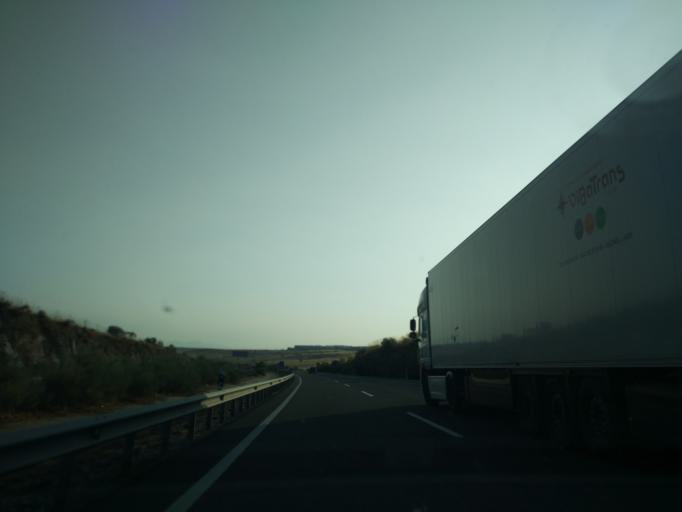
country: ES
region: Castille and Leon
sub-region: Provincia de Avila
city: Berrocalejo de Aragona
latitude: 40.6870
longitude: -4.5948
